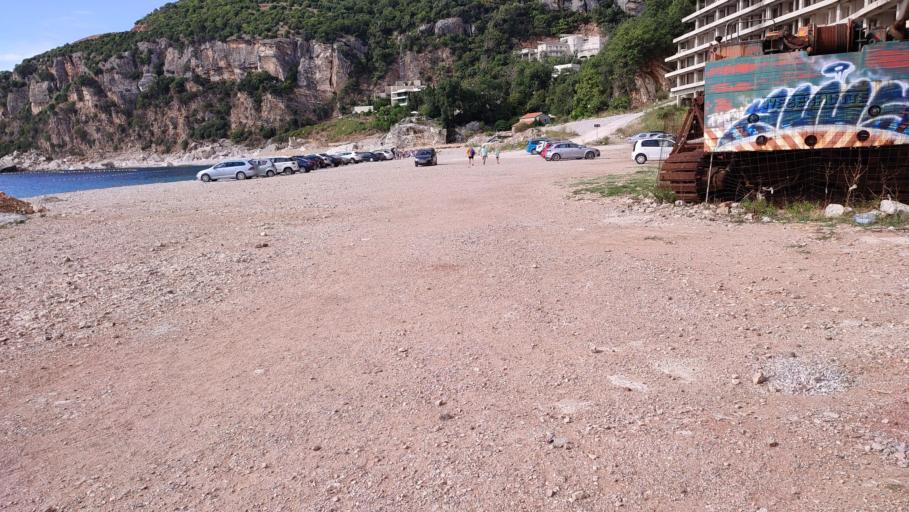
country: ME
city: Petrovac na Moru
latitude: 42.2100
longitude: 18.9260
